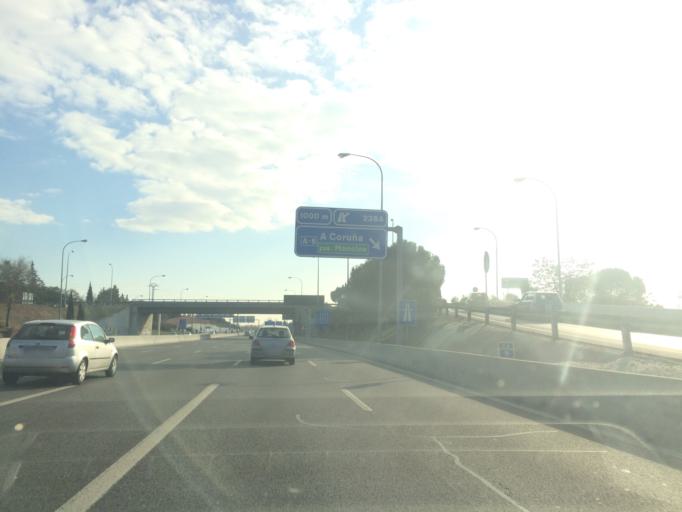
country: ES
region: Madrid
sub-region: Provincia de Madrid
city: Tetuan de las Victorias
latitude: 40.4701
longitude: -3.7504
